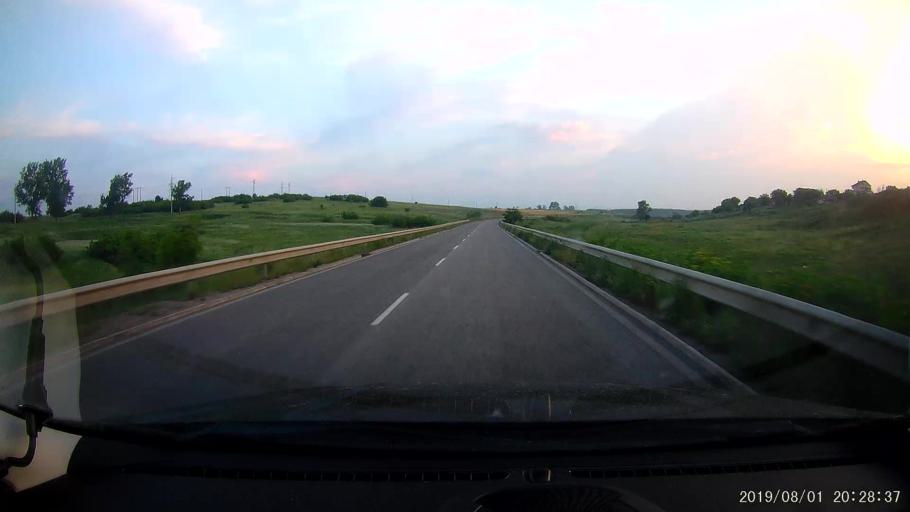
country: BG
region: Yambol
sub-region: Obshtina Elkhovo
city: Elkhovo
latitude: 42.1665
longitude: 26.5746
